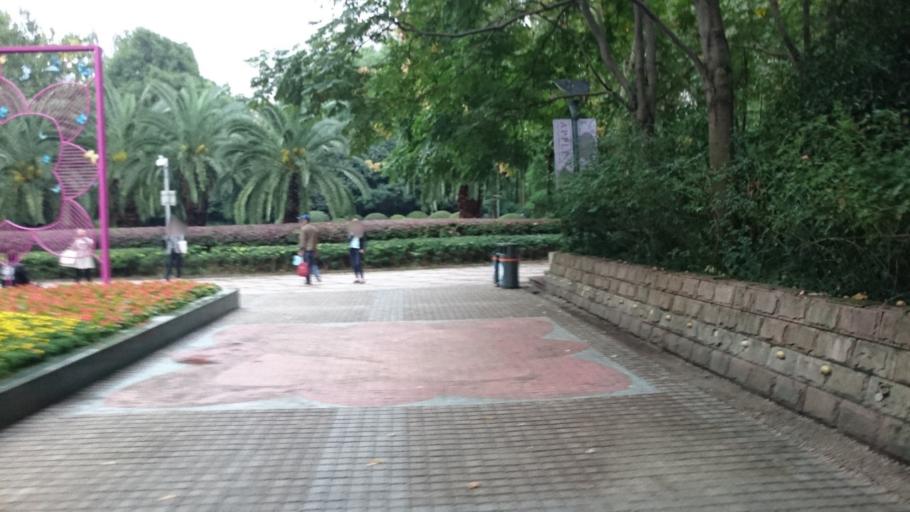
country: CN
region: Shanghai Shi
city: Shanghai
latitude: 31.2342
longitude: 121.4674
